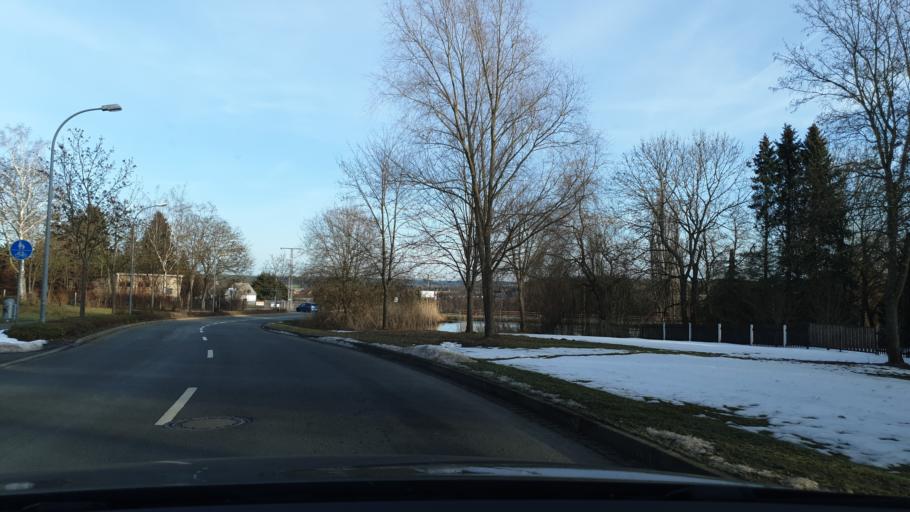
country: DE
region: Thuringia
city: Zeulenroda
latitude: 50.6428
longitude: 11.9798
